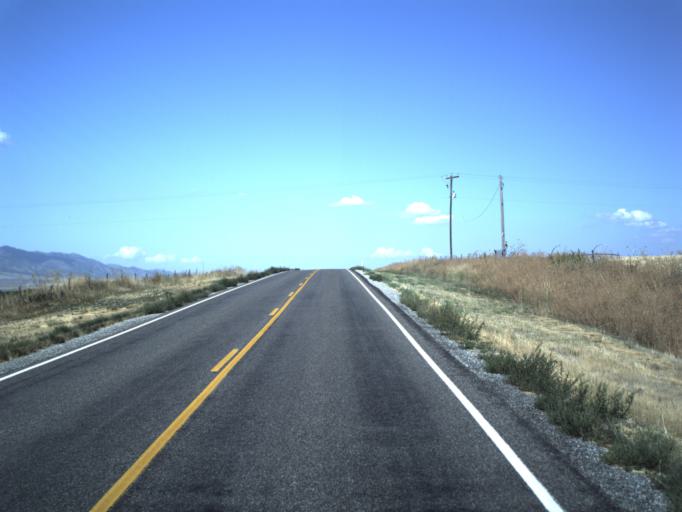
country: US
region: Utah
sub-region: Cache County
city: Benson
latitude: 41.8523
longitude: -111.9714
